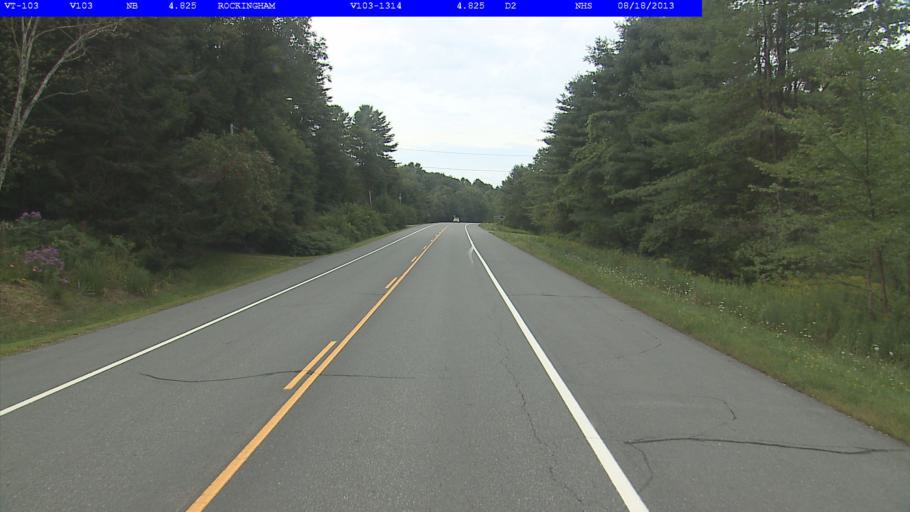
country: US
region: Vermont
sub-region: Windham County
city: Rockingham
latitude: 43.2112
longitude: -72.5381
